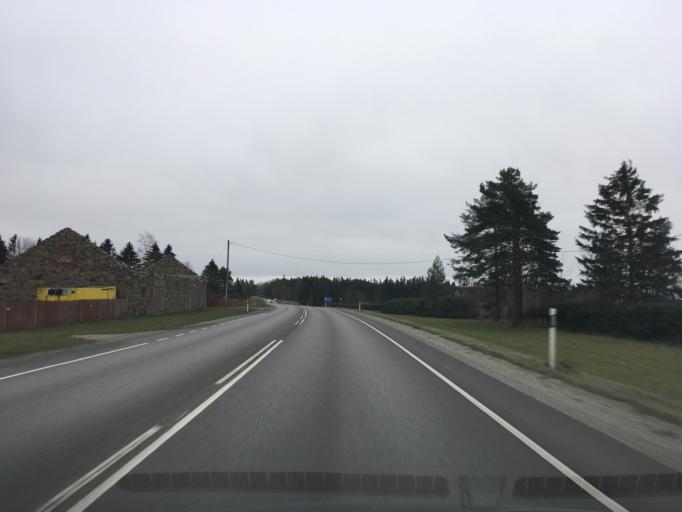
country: EE
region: Laeaene-Virumaa
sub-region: Rakvere linn
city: Rakvere
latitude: 59.4001
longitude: 26.3712
